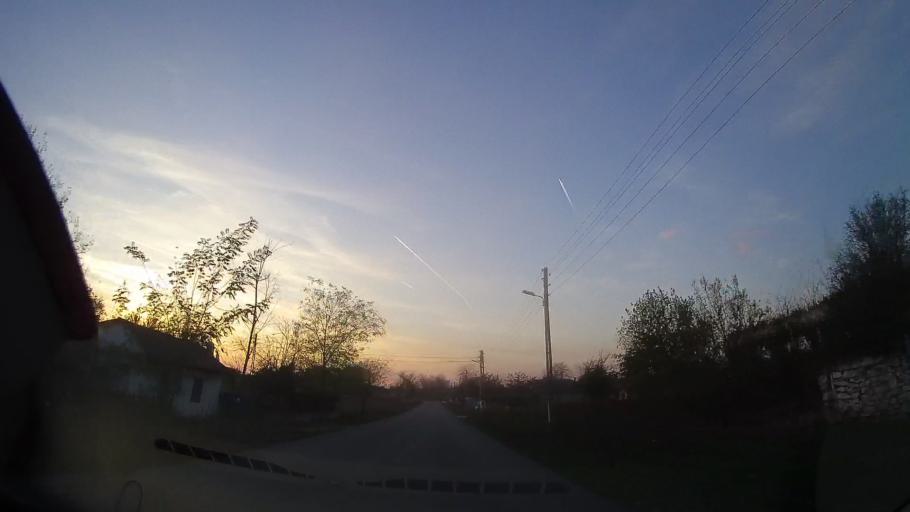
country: RO
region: Constanta
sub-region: Comuna Mereni
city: Mereni
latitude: 44.0147
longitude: 28.3259
